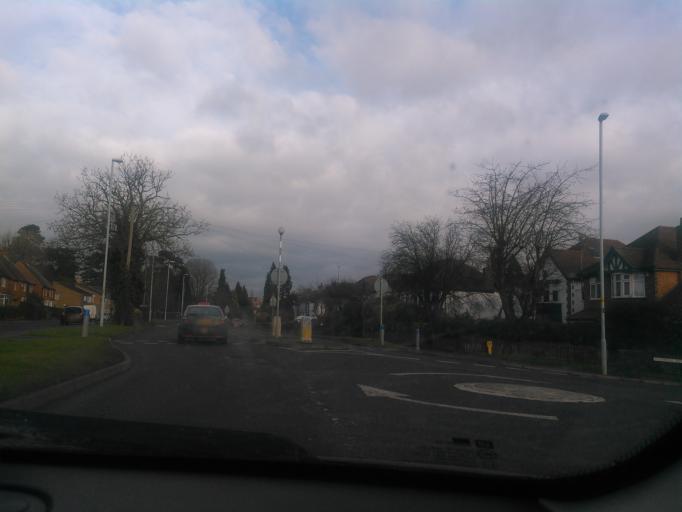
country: GB
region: England
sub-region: Leicestershire
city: Oadby
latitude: 52.5951
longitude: -1.0856
